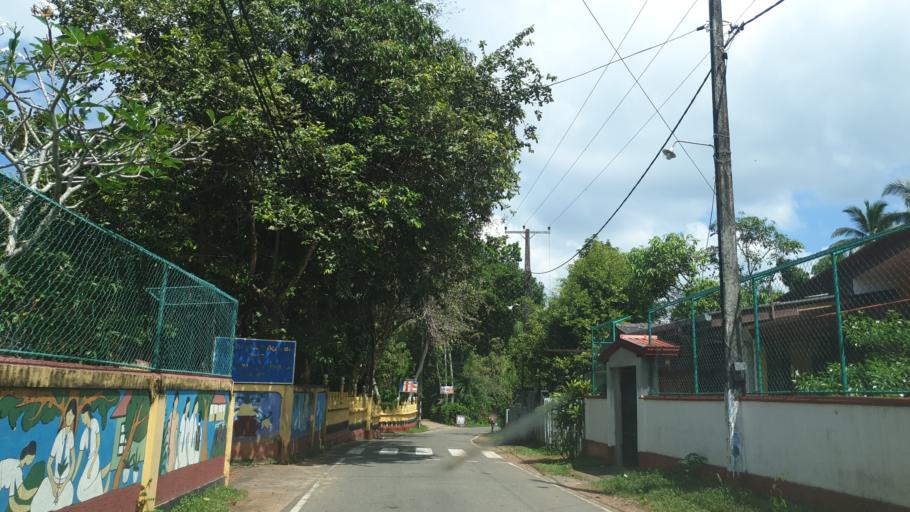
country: LK
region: Western
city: Panadura
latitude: 6.6805
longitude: 79.9406
